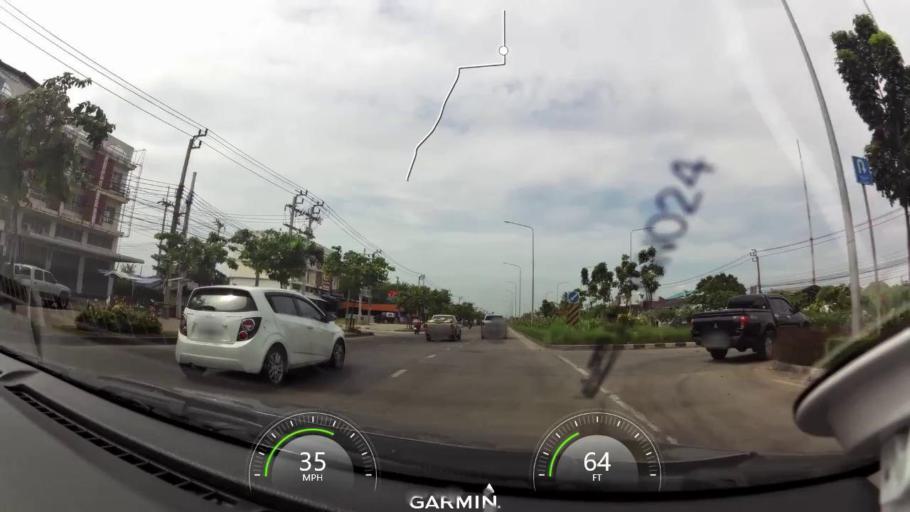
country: TH
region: Bangkok
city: Nong Khaem
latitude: 13.7161
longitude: 100.3641
